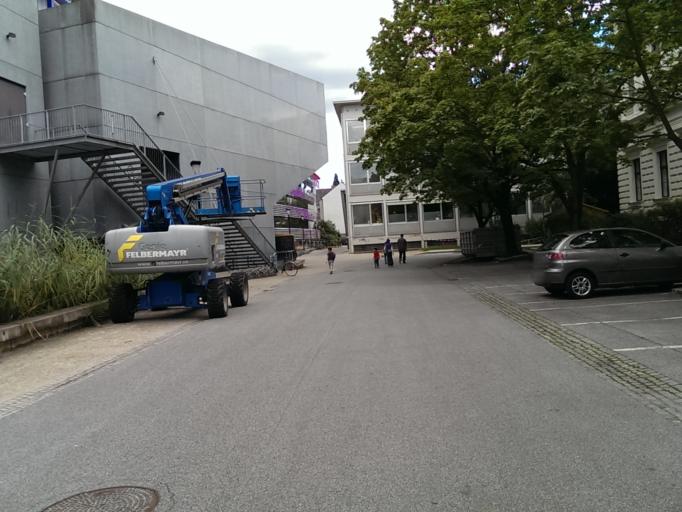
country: AT
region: Styria
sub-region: Graz Stadt
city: Graz
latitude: 47.0789
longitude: 15.4500
